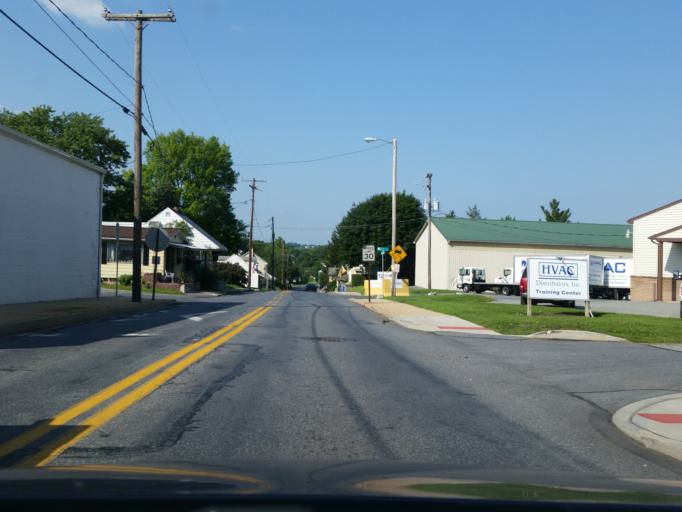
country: US
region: Pennsylvania
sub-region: Lancaster County
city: Mount Joy
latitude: 40.1115
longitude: -76.5058
